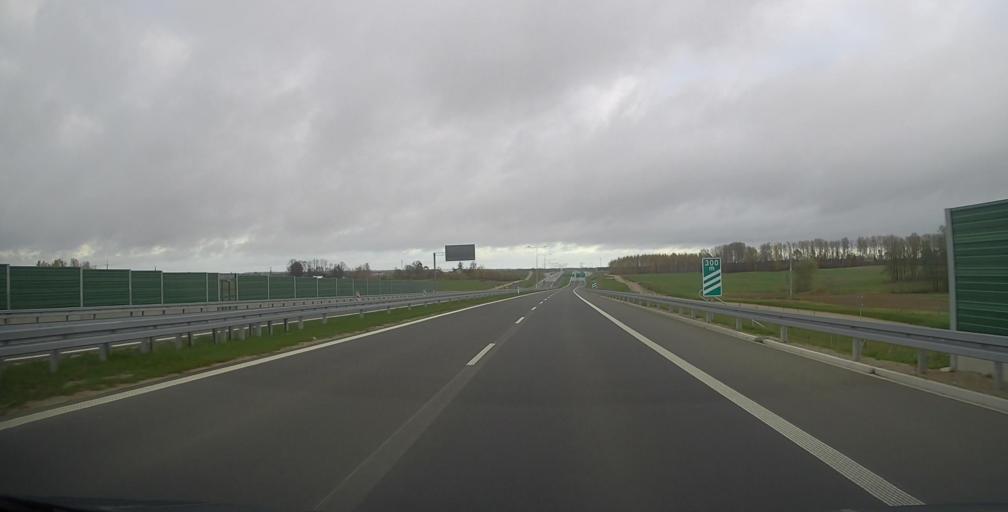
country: PL
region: Podlasie
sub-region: Powiat suwalski
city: Raczki
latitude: 53.9630
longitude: 22.7763
